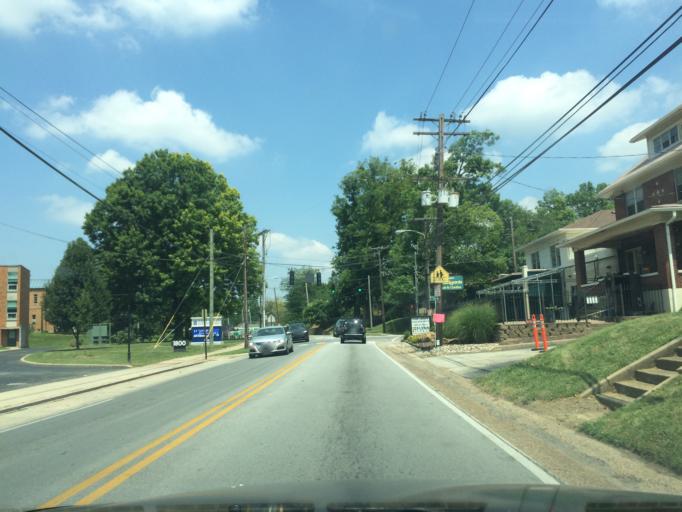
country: US
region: Kentucky
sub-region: Jefferson County
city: Audubon Park
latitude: 38.2225
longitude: -85.7106
